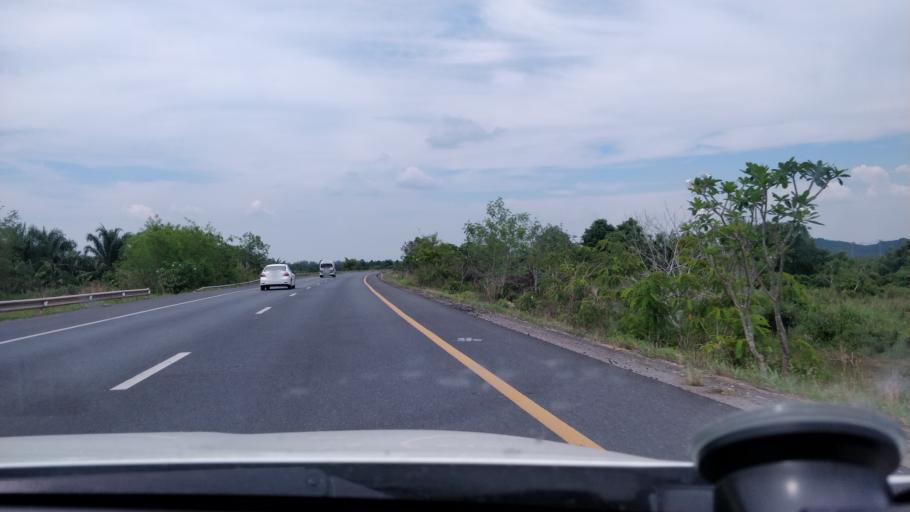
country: TH
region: Surat Thani
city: Khian Sa
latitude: 8.8502
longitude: 99.1809
